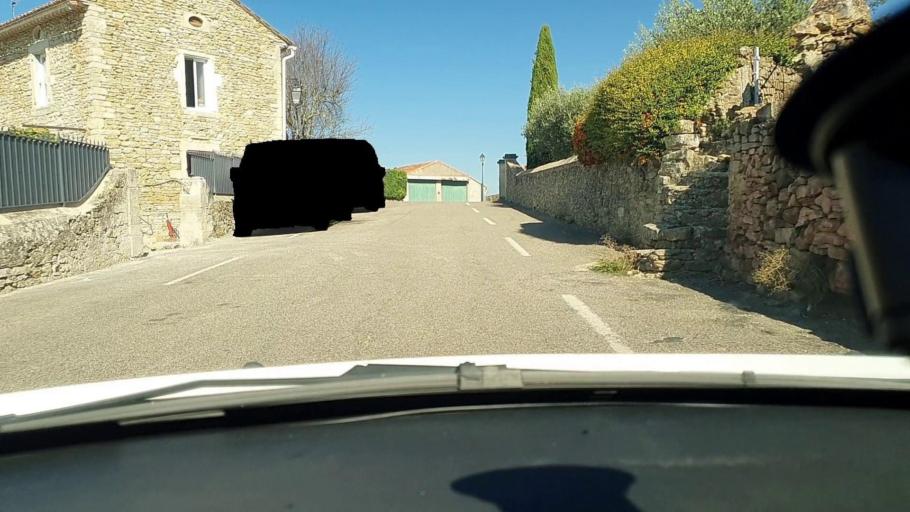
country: FR
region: Languedoc-Roussillon
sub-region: Departement du Gard
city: Saint-Julien-de-Peyrolas
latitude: 44.2599
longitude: 4.5247
